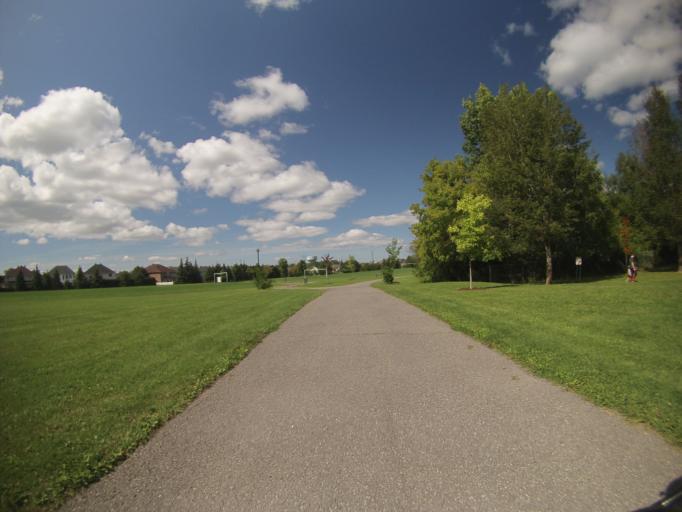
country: CA
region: Ontario
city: Ottawa
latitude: 45.3674
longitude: -75.6268
